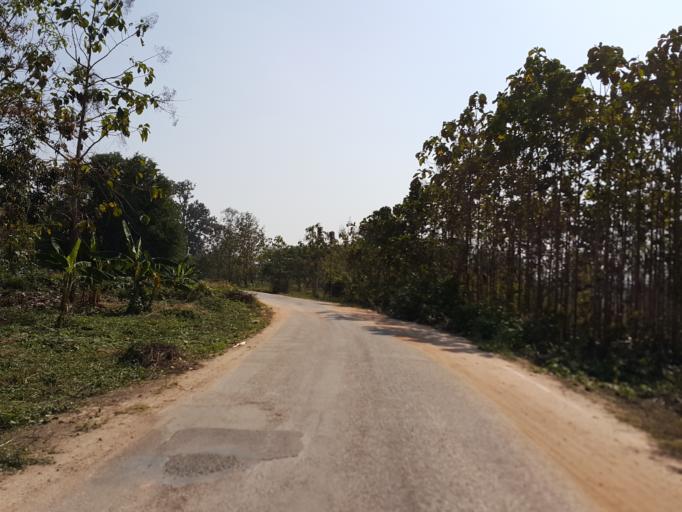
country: TH
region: Lampang
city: Wang Nuea
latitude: 19.0052
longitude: 99.6227
